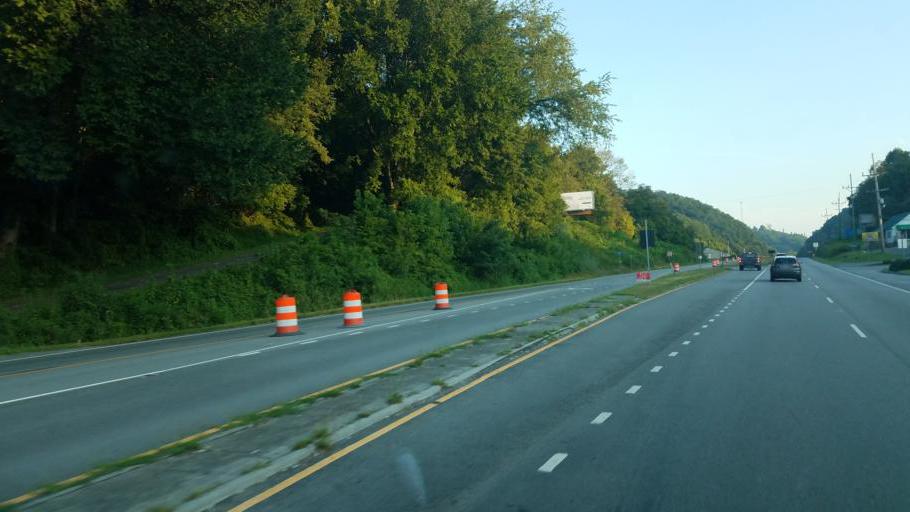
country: US
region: Virginia
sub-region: Scott County
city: Weber City
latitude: 36.6064
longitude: -82.5694
